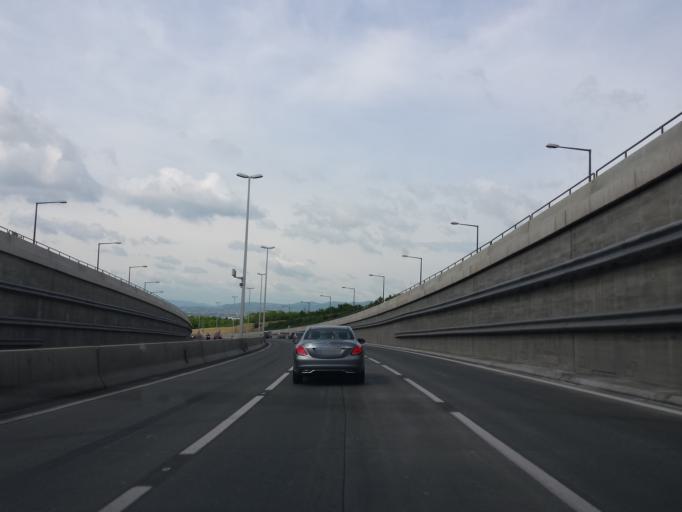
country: AT
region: Lower Austria
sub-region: Politischer Bezirk Wien-Umgebung
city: Leopoldsdorf
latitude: 48.1598
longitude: 16.3794
